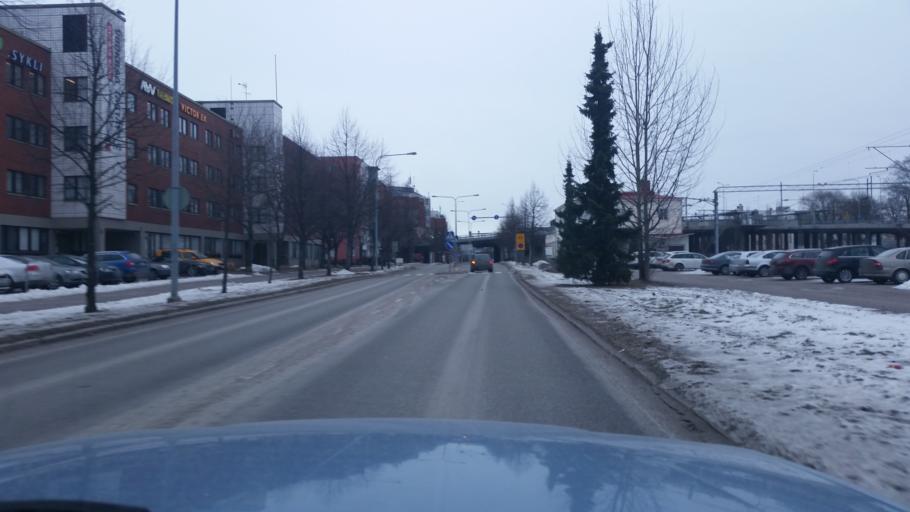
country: FI
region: Uusimaa
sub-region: Helsinki
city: Vantaa
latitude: 60.2491
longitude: 25.0060
